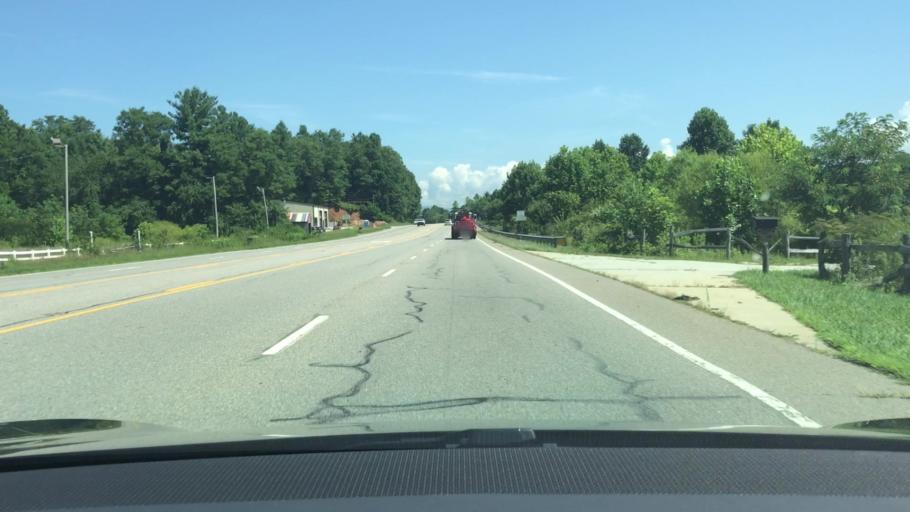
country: US
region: North Carolina
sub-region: Macon County
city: Franklin
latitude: 35.0865
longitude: -83.3837
